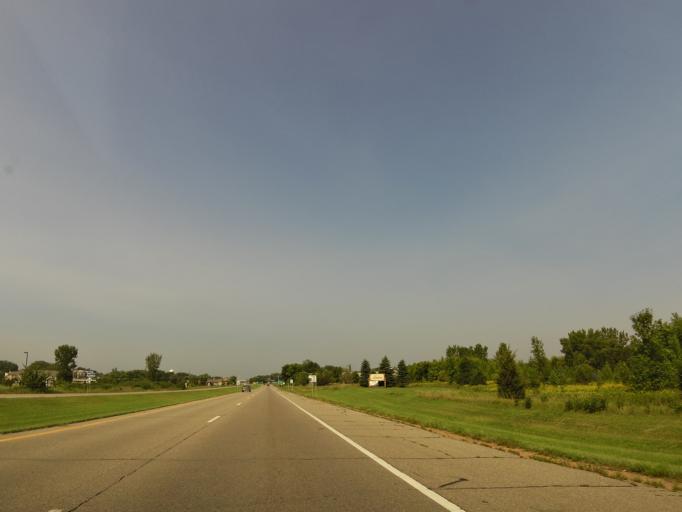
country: US
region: Minnesota
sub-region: Carver County
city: Norwood Young America
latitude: 44.7689
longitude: -93.9117
